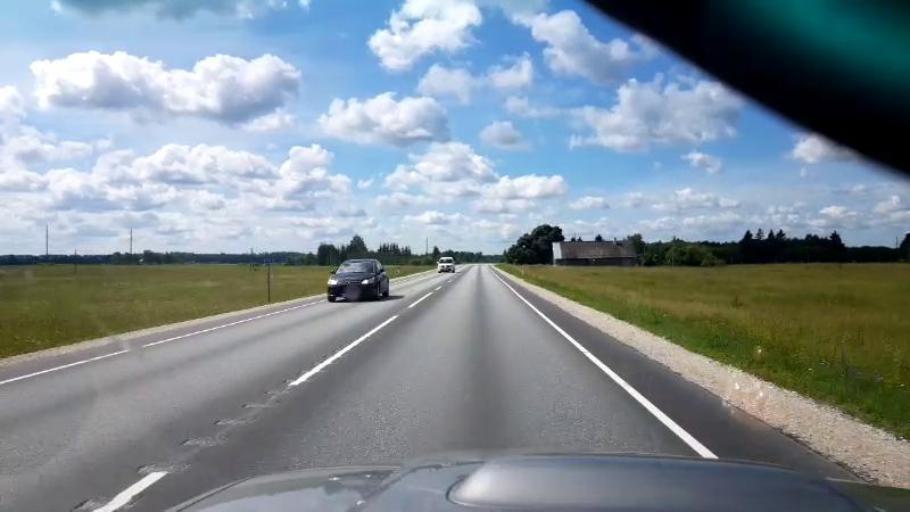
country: EE
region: Laeaene-Virumaa
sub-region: Tapa vald
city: Tapa
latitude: 59.2727
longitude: 26.0365
